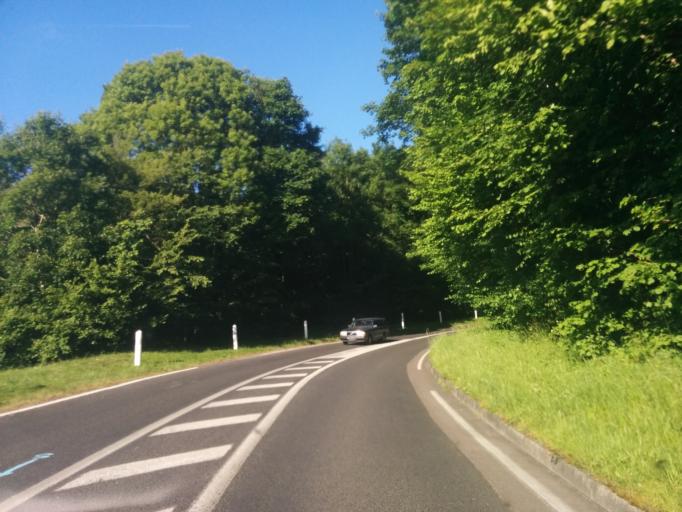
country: FR
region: Haute-Normandie
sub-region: Departement de l'Eure
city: Vernon
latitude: 49.0996
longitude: 1.5032
